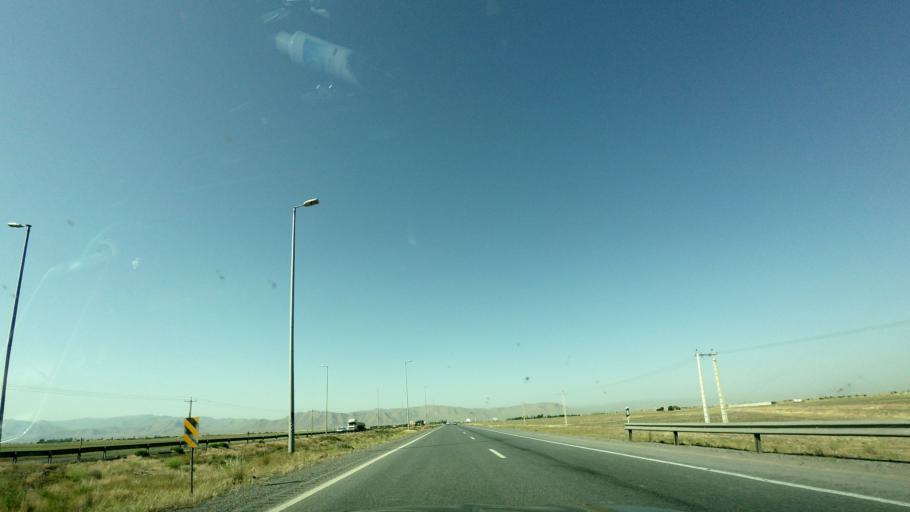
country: IR
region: Markazi
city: Ashtian
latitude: 34.1928
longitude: 50.0557
